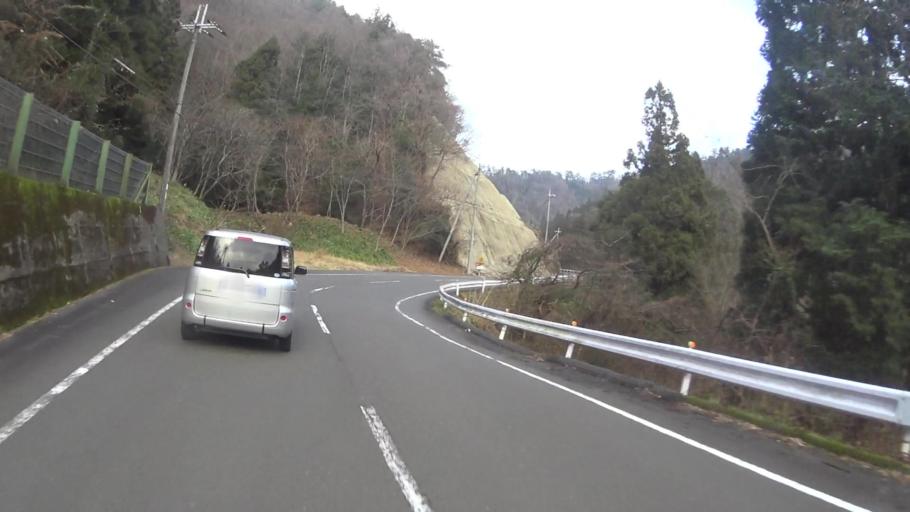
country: JP
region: Kyoto
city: Maizuru
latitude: 35.4338
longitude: 135.3914
